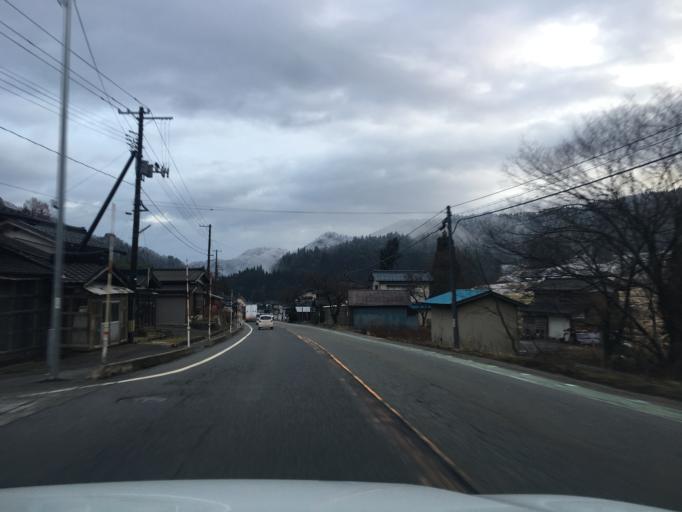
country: JP
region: Niigata
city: Murakami
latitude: 38.3856
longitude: 139.5545
